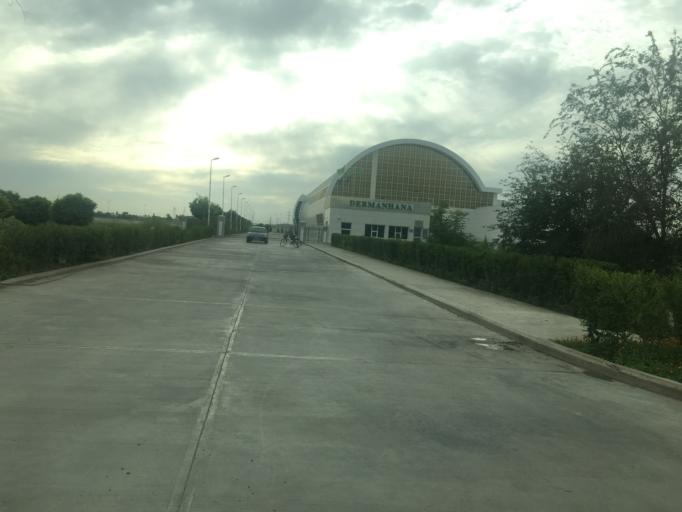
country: TM
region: Dasoguz
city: Dasoguz
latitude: 41.8304
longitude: 59.9242
